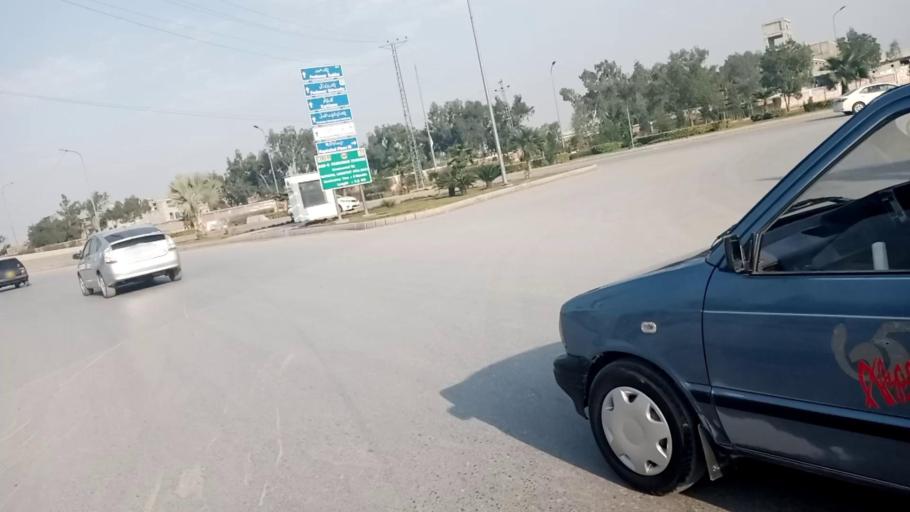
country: PK
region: Khyber Pakhtunkhwa
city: Peshawar
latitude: 33.9929
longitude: 71.4569
